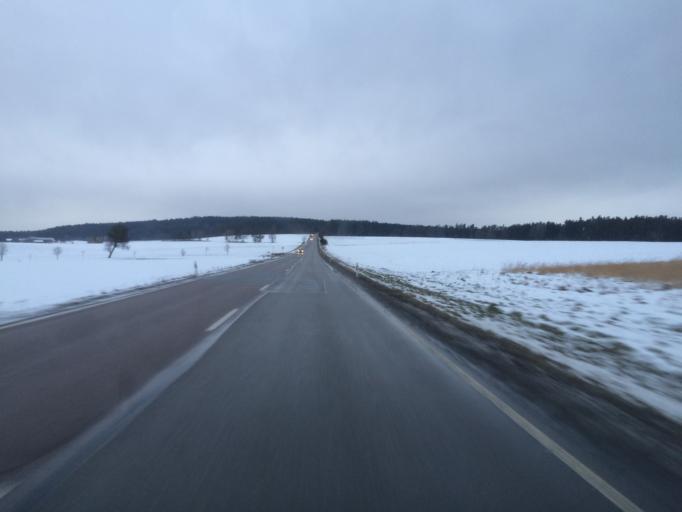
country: DE
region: Bavaria
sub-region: Upper Palatinate
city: Breitenbrunn
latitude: 49.3548
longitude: 12.0609
